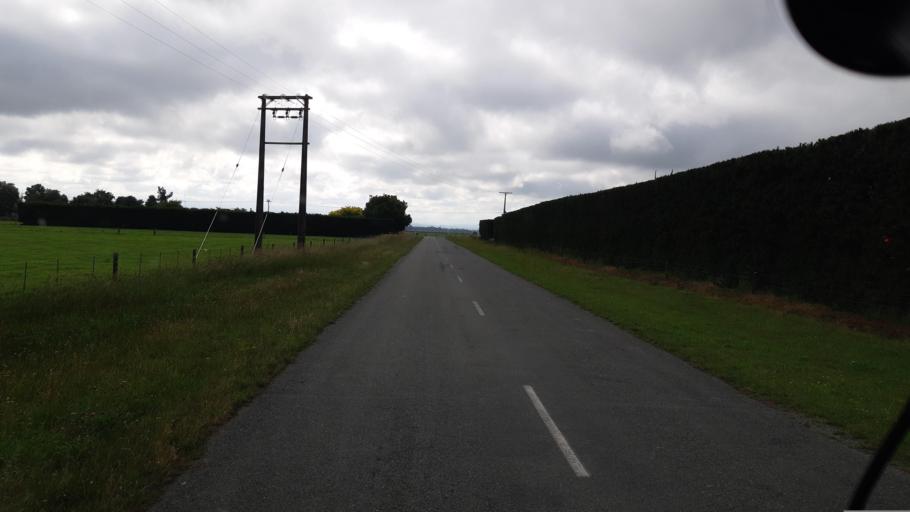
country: NZ
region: Canterbury
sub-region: Timaru District
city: Timaru
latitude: -44.2397
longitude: 171.3485
